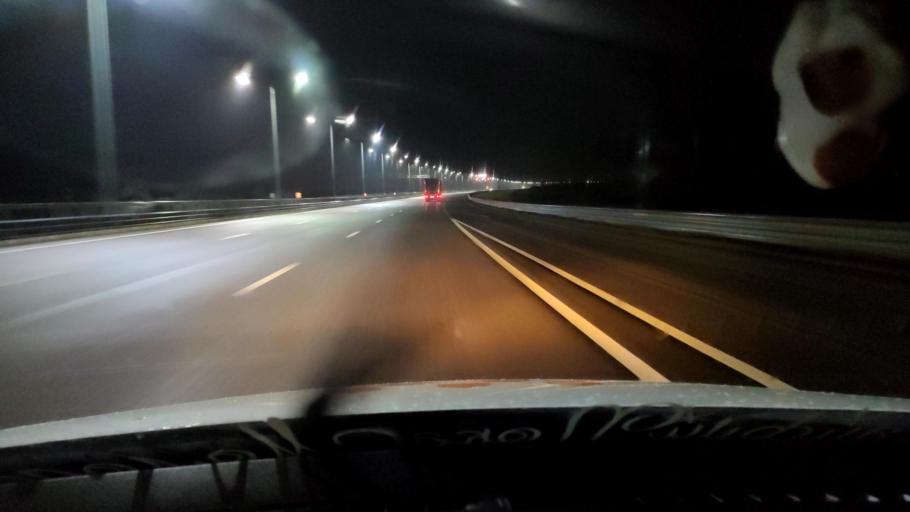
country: RU
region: Voronezj
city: Somovo
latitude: 51.7776
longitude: 39.2979
